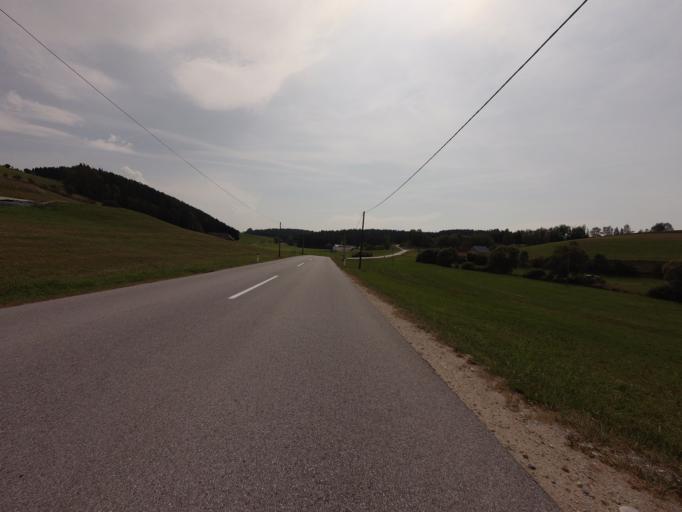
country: AT
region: Upper Austria
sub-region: Politischer Bezirk Urfahr-Umgebung
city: Reichenthal
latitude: 48.5475
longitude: 14.3966
